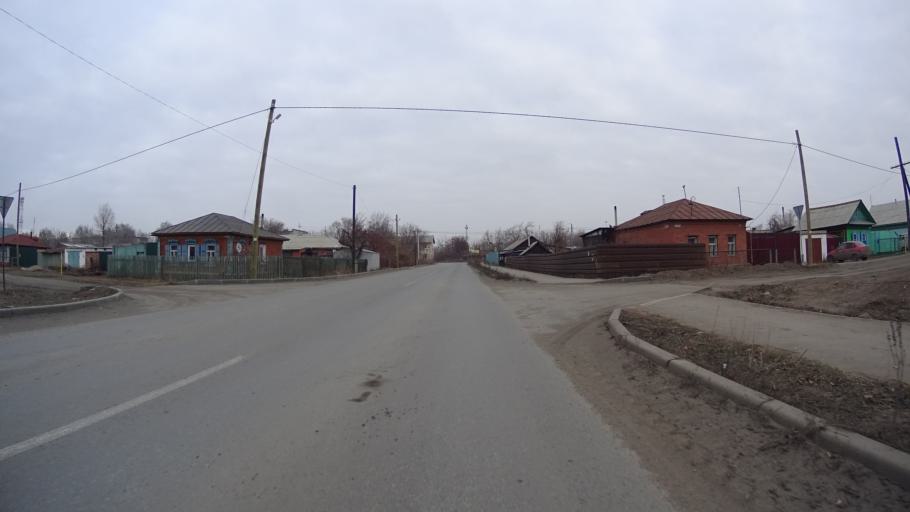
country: RU
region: Chelyabinsk
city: Troitsk
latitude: 54.1075
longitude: 61.5708
